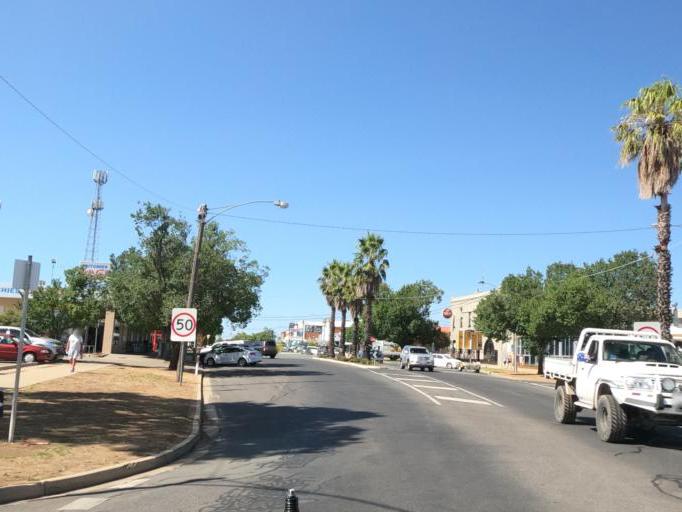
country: AU
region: Victoria
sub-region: Moira
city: Yarrawonga
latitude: -36.0082
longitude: 146.0046
